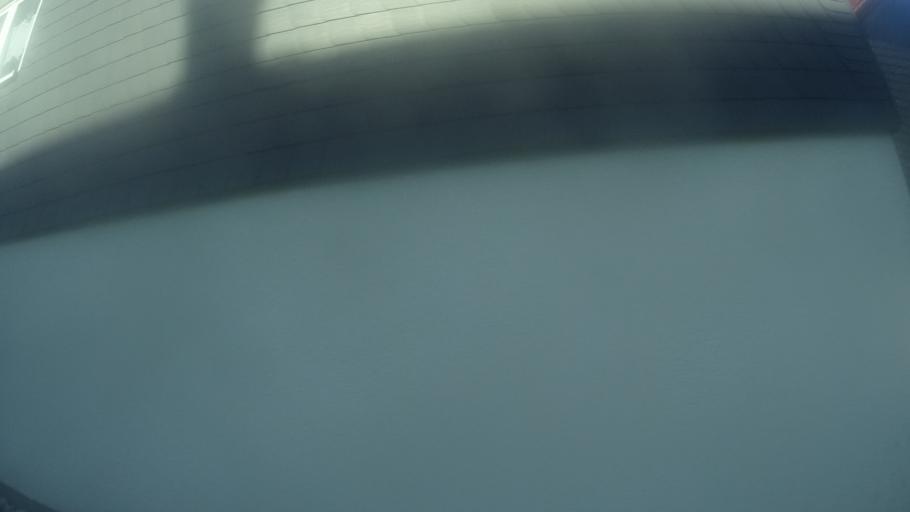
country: DE
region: Thuringia
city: Oberhain
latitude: 50.6292
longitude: 11.1232
